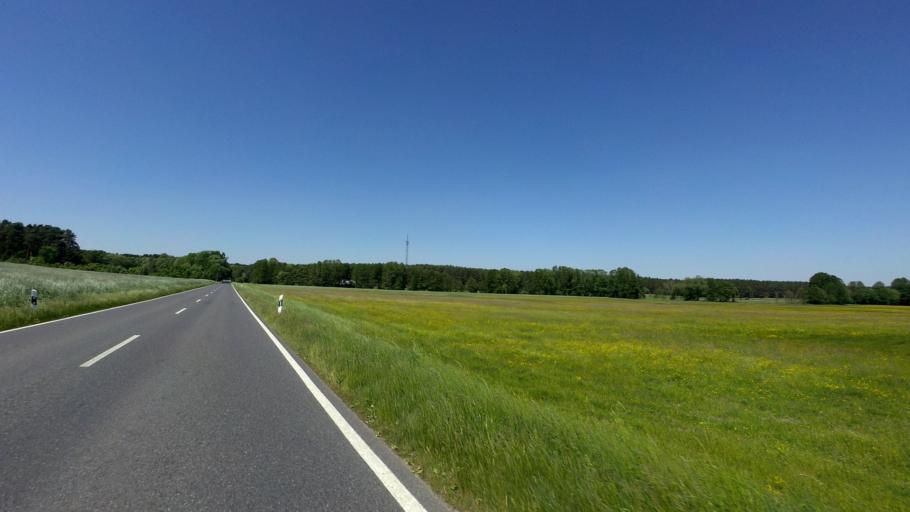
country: DE
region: Brandenburg
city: Lieberose
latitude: 51.9858
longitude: 14.2140
